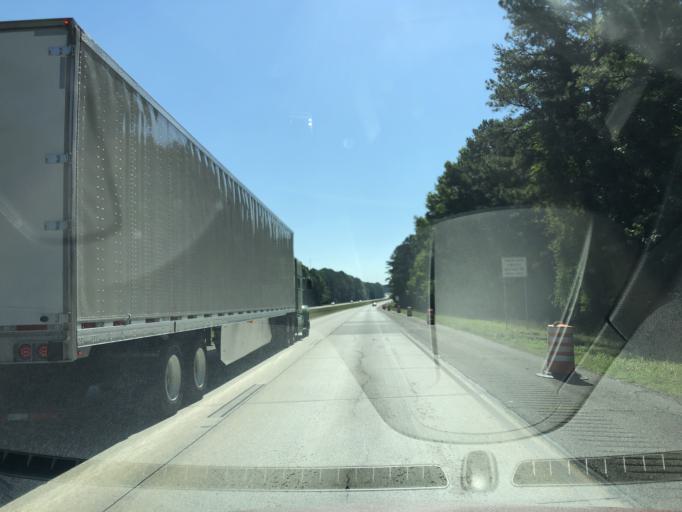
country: US
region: Georgia
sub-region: Taliaferro County
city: Crawfordville
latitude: 33.4996
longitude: -82.7976
